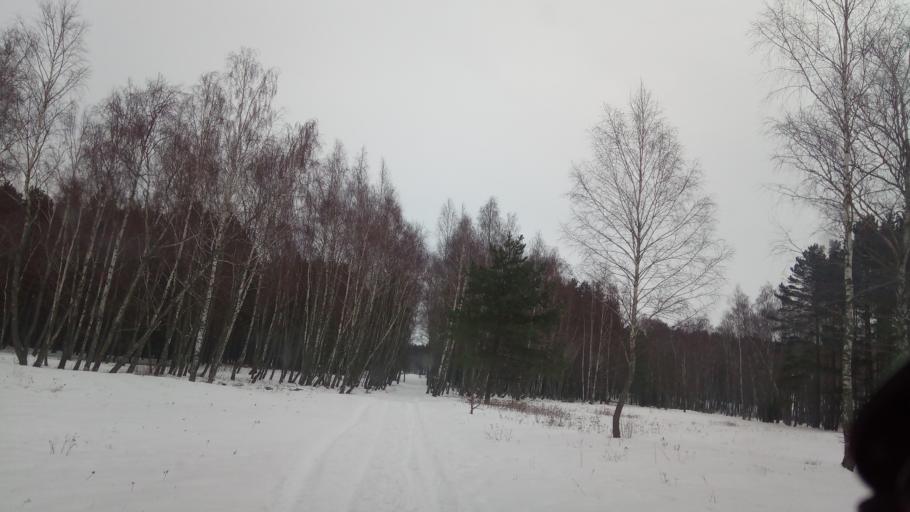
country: LT
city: Neringa
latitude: 55.4186
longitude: 21.1035
